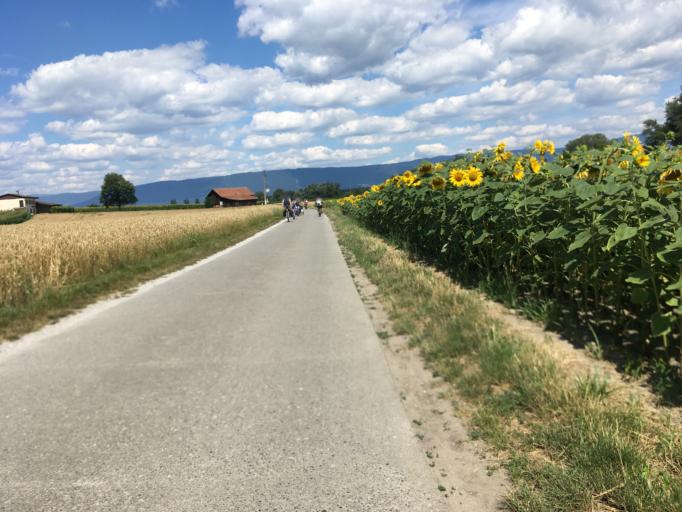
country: CH
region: Fribourg
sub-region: See District
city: Bas-Vully
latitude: 46.9672
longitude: 7.1083
